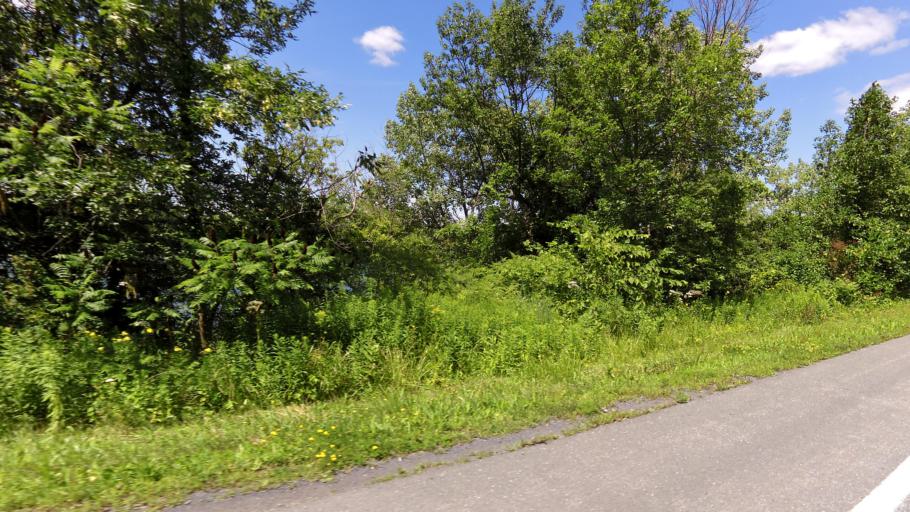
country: CA
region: Quebec
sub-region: Monteregie
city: Richelieu
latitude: 45.4268
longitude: -73.2446
